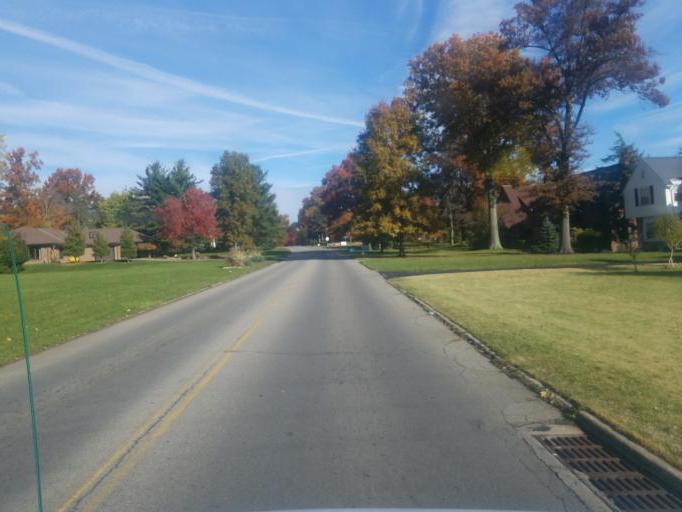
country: US
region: Ohio
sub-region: Richland County
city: Mansfield
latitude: 40.7412
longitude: -82.5407
